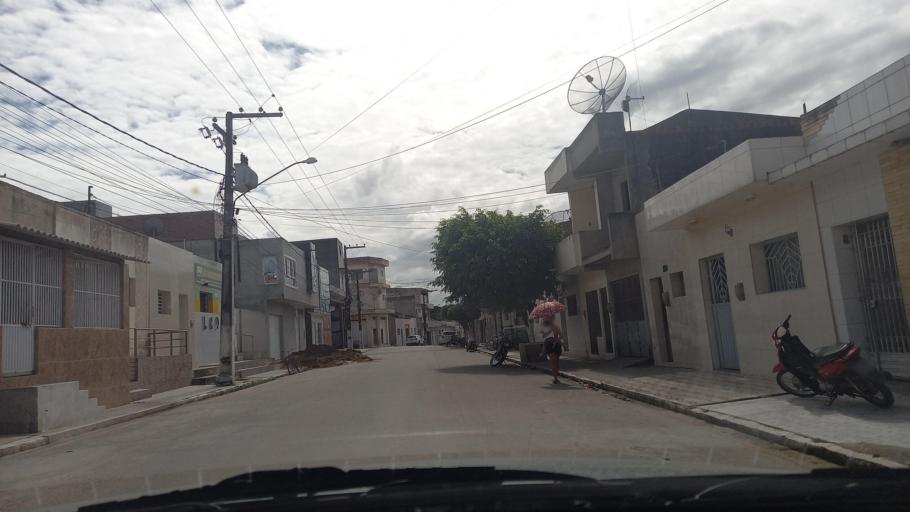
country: BR
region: Pernambuco
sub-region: Cachoeirinha
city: Cachoeirinha
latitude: -8.4901
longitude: -36.2336
